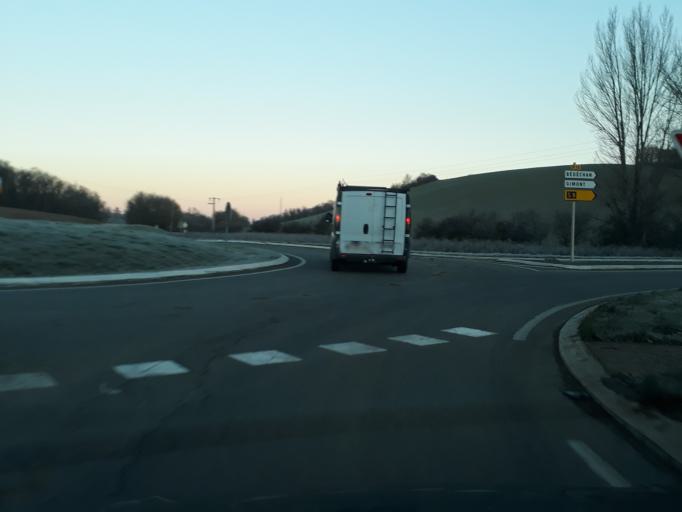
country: FR
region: Midi-Pyrenees
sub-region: Departement du Gers
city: Aubiet
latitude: 43.5590
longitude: 0.7961
